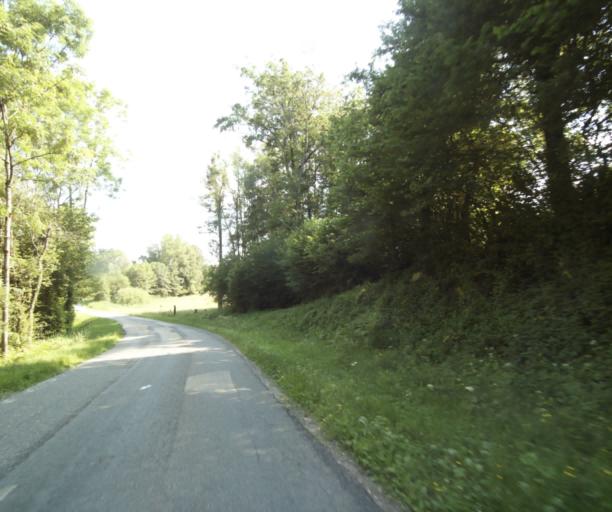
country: FR
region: Rhone-Alpes
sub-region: Departement de la Haute-Savoie
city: Allinges
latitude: 46.3317
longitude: 6.4924
